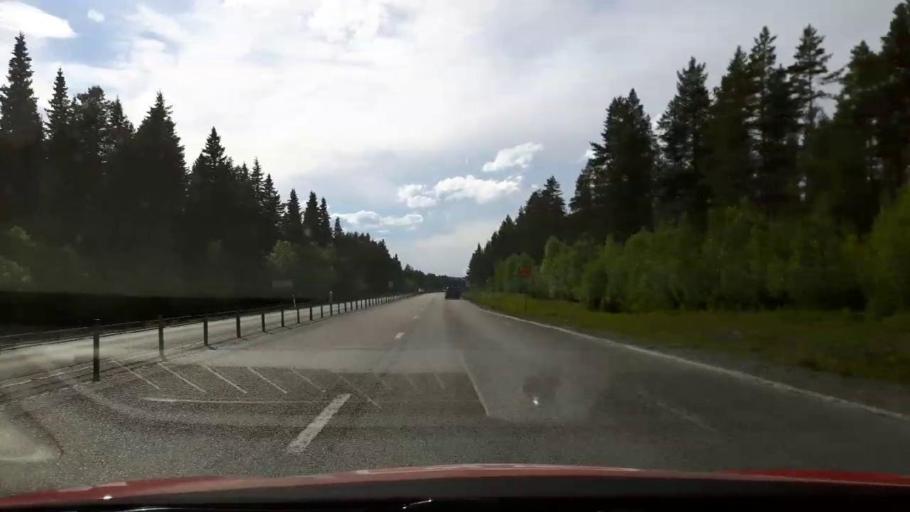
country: SE
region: Jaemtland
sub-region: OEstersunds Kommun
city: Ostersund
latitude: 63.1747
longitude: 14.6982
